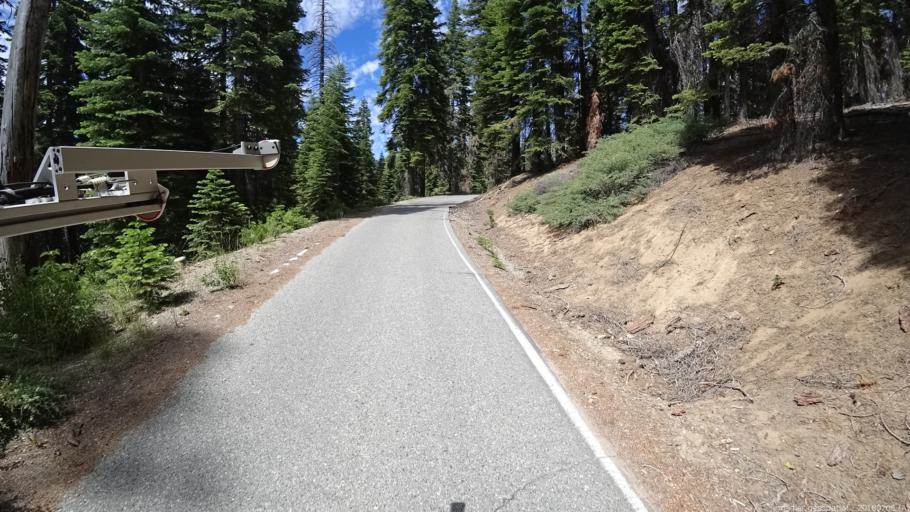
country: US
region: California
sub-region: Madera County
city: Oakhurst
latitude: 37.4391
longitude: -119.4357
